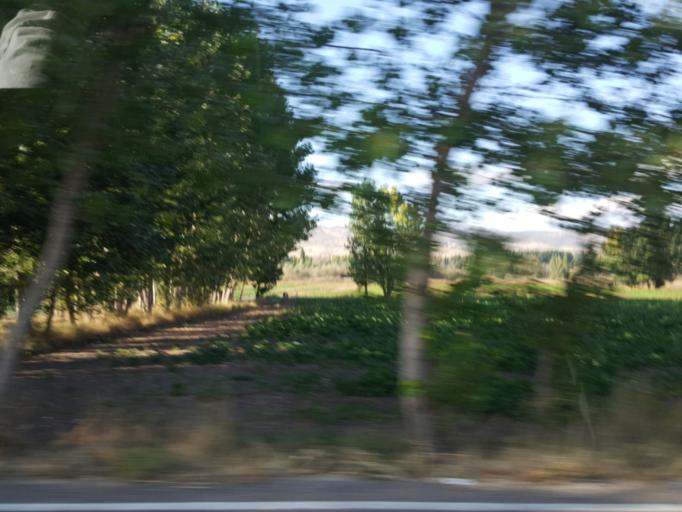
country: TR
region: Tokat
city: Yesilyurt
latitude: 40.0179
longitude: 36.2557
